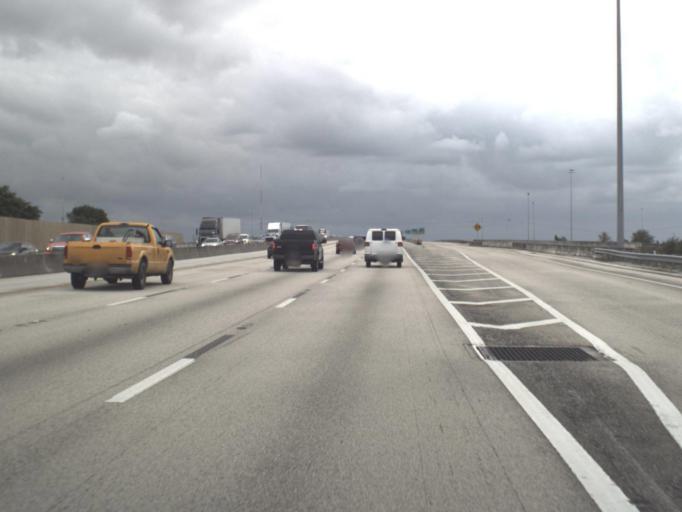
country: US
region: Florida
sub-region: Palm Beach County
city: Villages of Oriole
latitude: 26.5328
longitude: -80.1728
